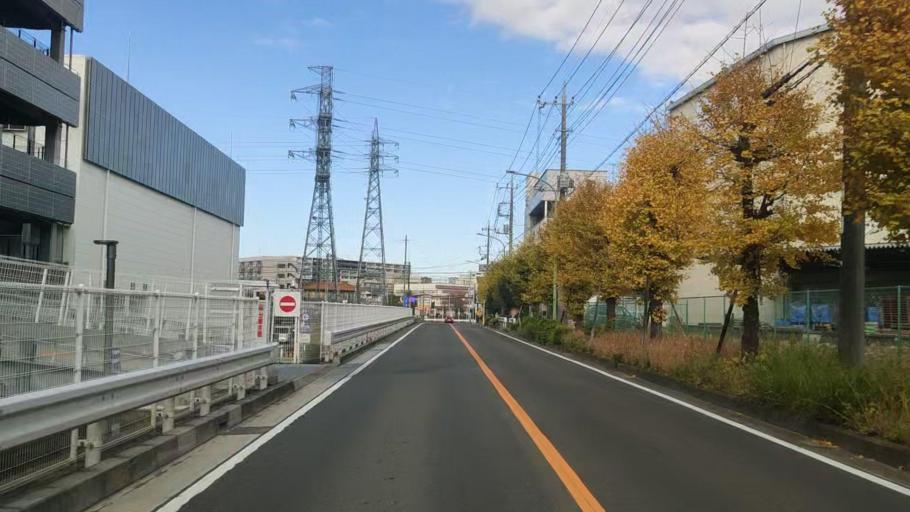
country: JP
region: Kanagawa
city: Minami-rinkan
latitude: 35.5002
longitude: 139.4260
